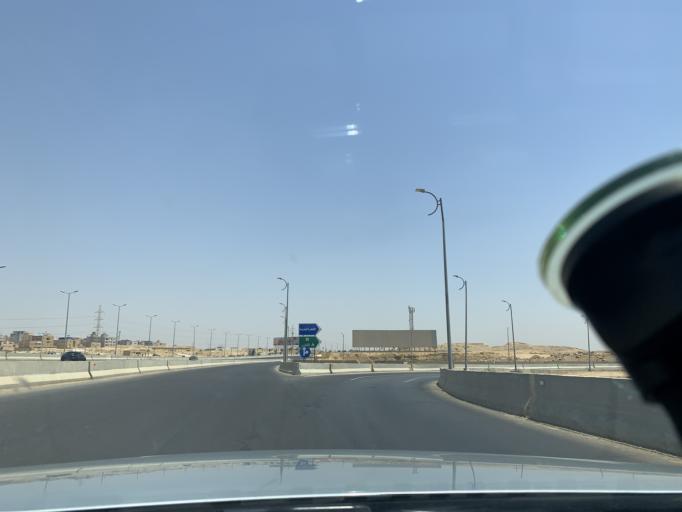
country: EG
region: Muhafazat al Qahirah
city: Halwan
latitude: 29.9666
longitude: 31.4710
